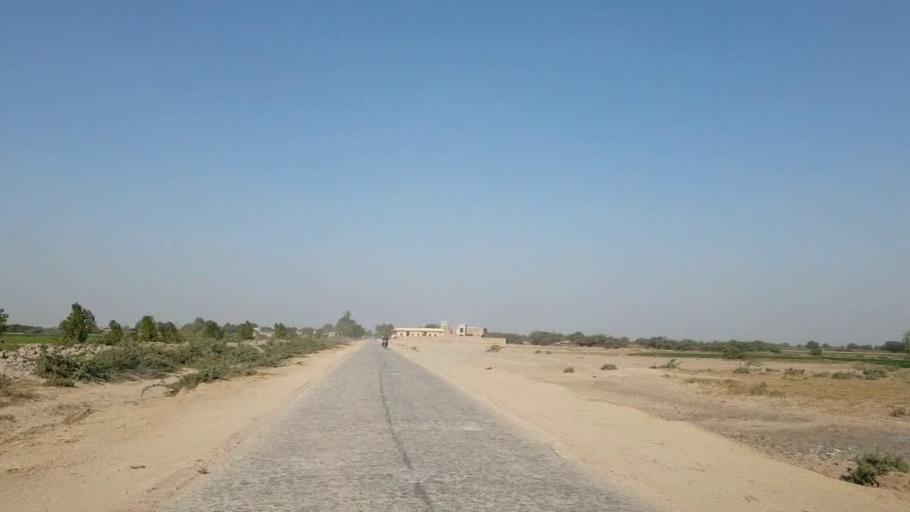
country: PK
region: Sindh
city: Digri
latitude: 25.1267
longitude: 69.1101
